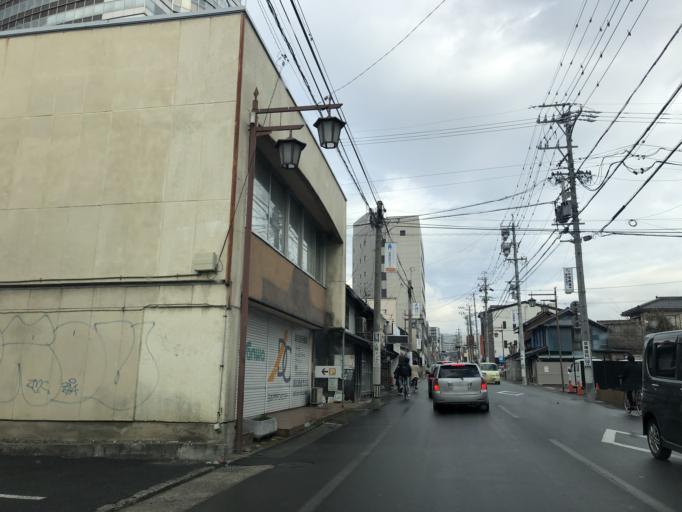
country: JP
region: Nagano
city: Nagano-shi
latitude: 36.6477
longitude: 138.1923
